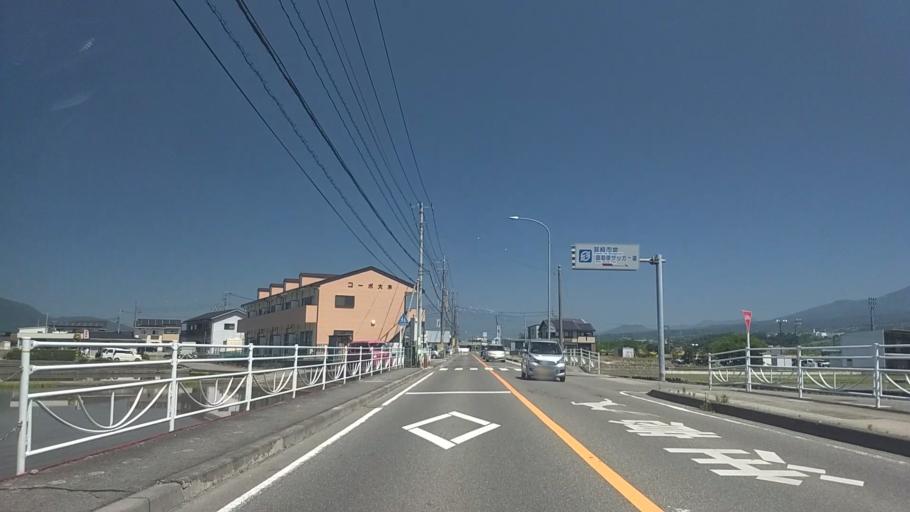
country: JP
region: Yamanashi
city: Nirasaki
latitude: 35.6881
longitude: 138.4617
